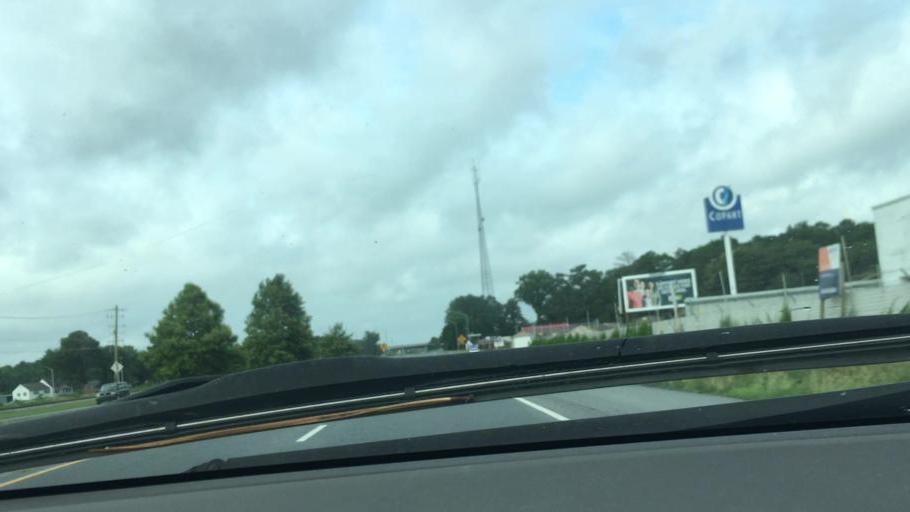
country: US
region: Maryland
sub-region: Wicomico County
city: Fruitland
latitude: 38.3094
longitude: -75.6292
